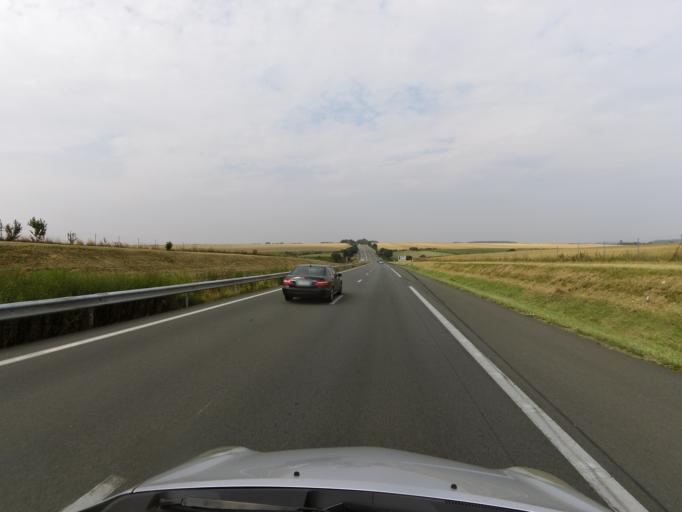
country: FR
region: Nord-Pas-de-Calais
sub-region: Departement du Nord
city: Gouzeaucourt
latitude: 50.0481
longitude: 3.1773
